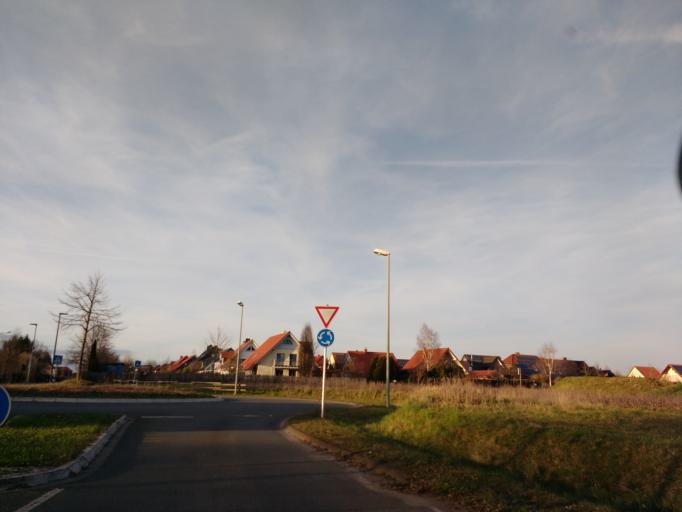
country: DE
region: North Rhine-Westphalia
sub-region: Regierungsbezirk Detmold
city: Salzkotten
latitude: 51.6664
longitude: 8.6158
